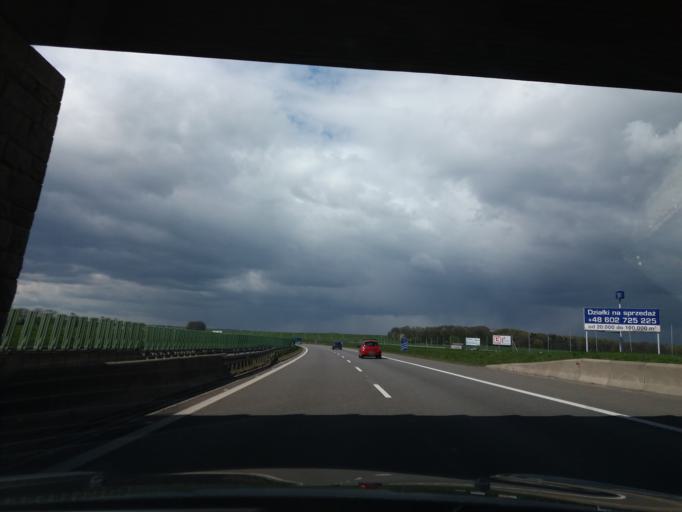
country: PL
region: Opole Voivodeship
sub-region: Powiat strzelecki
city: Strzelce Opolskie
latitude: 50.4582
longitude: 18.2832
